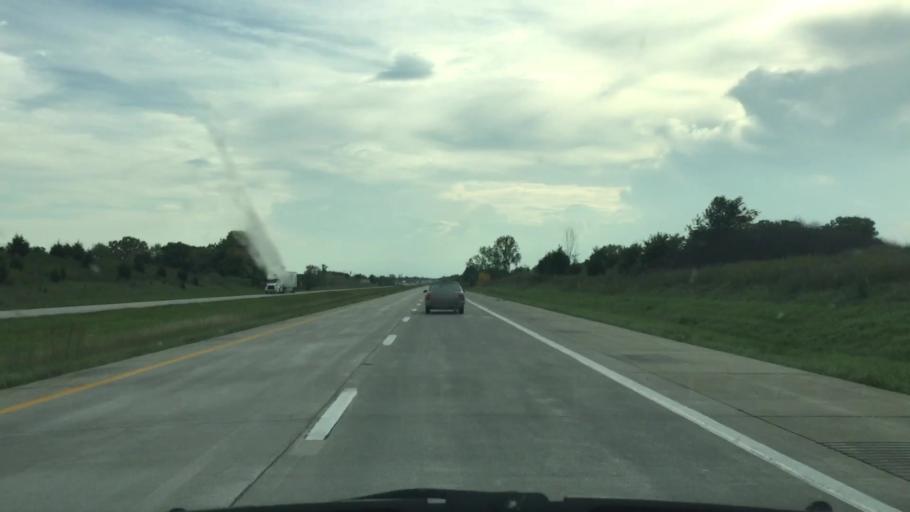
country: US
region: Missouri
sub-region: Harrison County
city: Bethany
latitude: 40.1695
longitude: -94.0233
